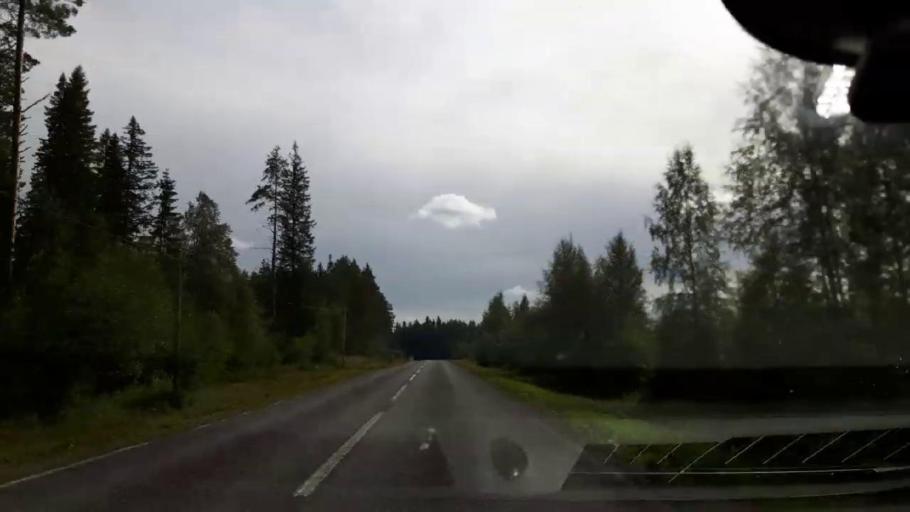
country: SE
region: Jaemtland
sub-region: Ragunda Kommun
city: Hammarstrand
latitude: 63.1420
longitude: 15.8601
